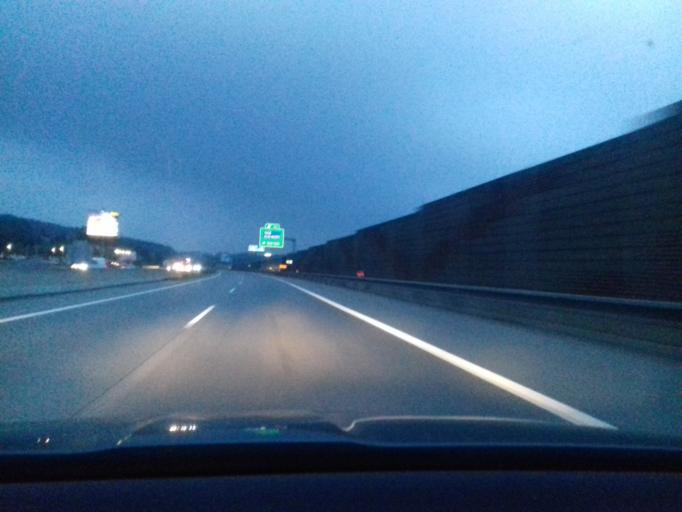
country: CZ
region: Vysocina
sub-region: Okres Zd'ar nad Sazavou
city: Velke Mezirici
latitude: 49.3483
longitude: 16.0389
